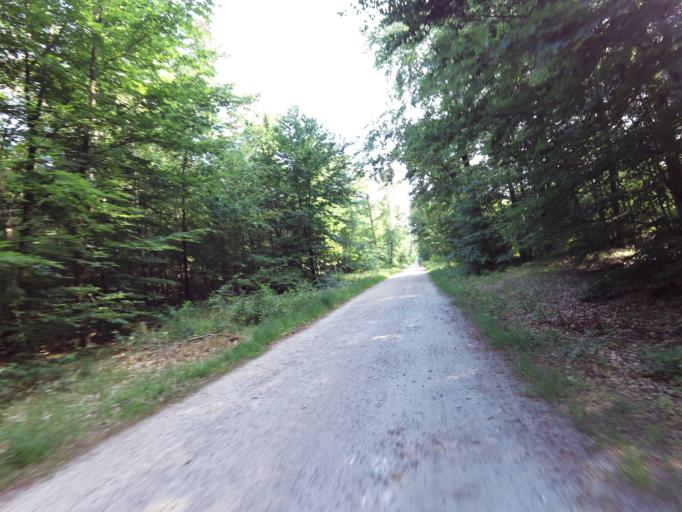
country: DE
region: Lower Saxony
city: Nordholz
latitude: 53.8470
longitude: 8.5932
